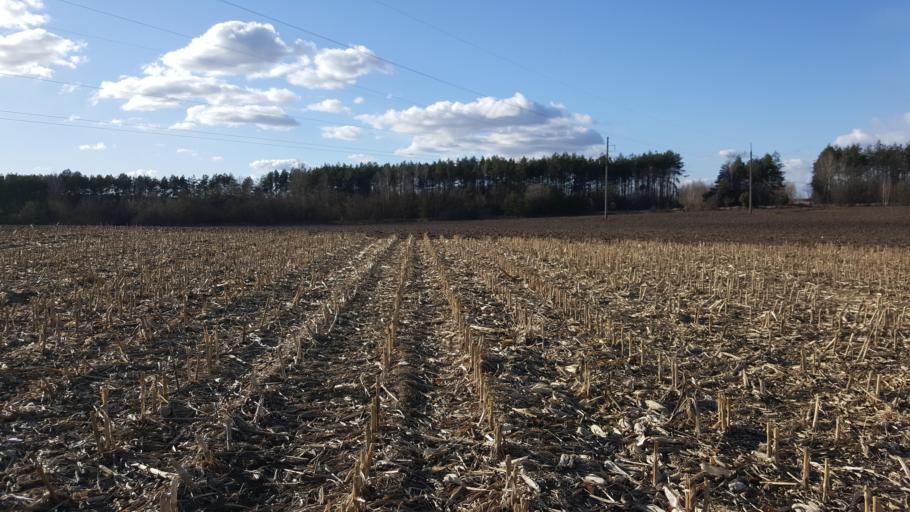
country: BY
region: Brest
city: Kamyanyets
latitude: 52.3834
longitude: 23.8474
